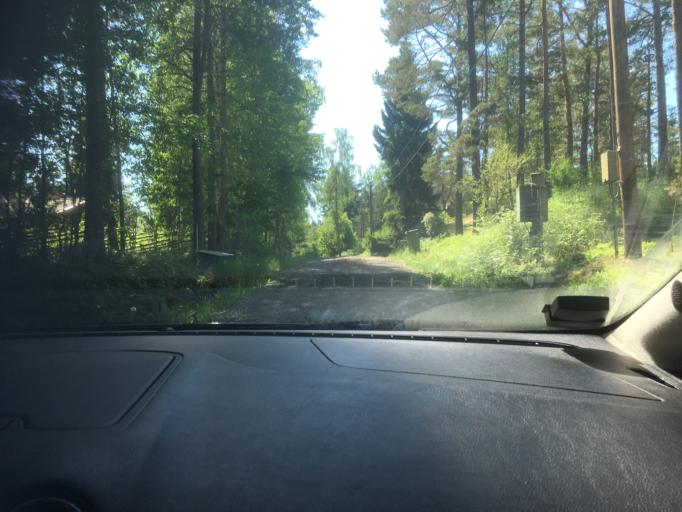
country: SE
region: Stockholm
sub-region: Haninge Kommun
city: Jordbro
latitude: 59.0136
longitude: 18.1612
